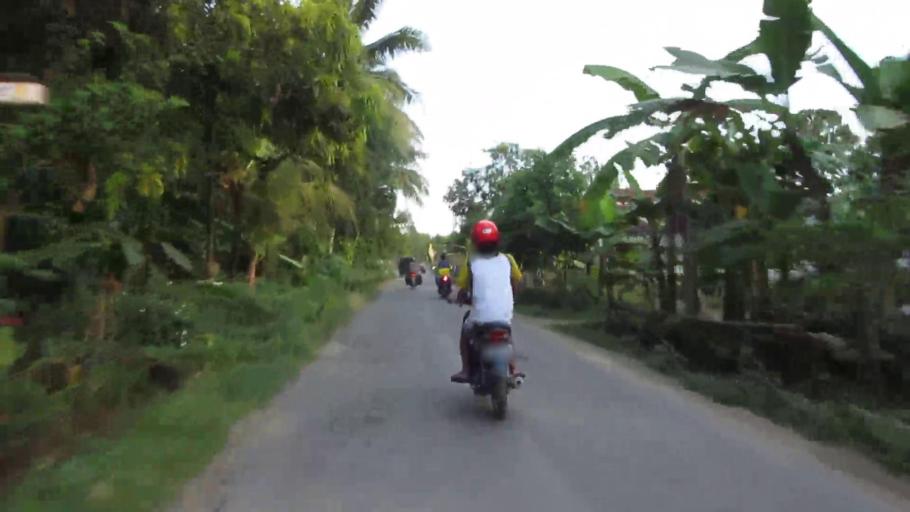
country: ID
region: West Java
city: Karangjaladri
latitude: -7.7092
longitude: 108.4969
